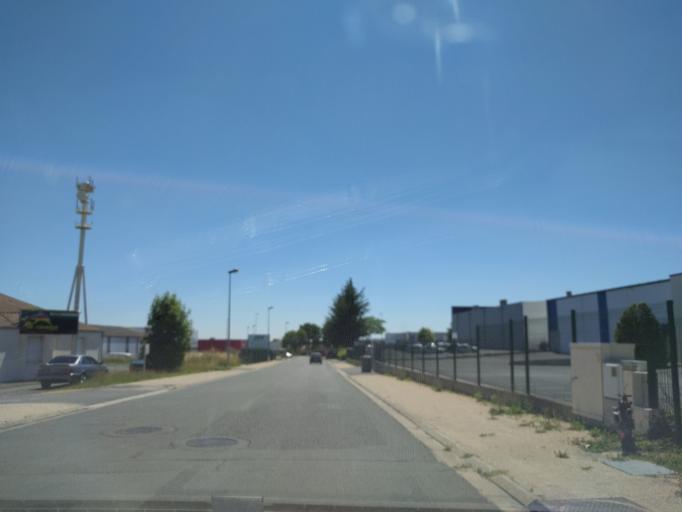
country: FR
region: Poitou-Charentes
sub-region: Departement des Deux-Sevres
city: Chauray
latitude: 46.3377
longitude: -0.4024
